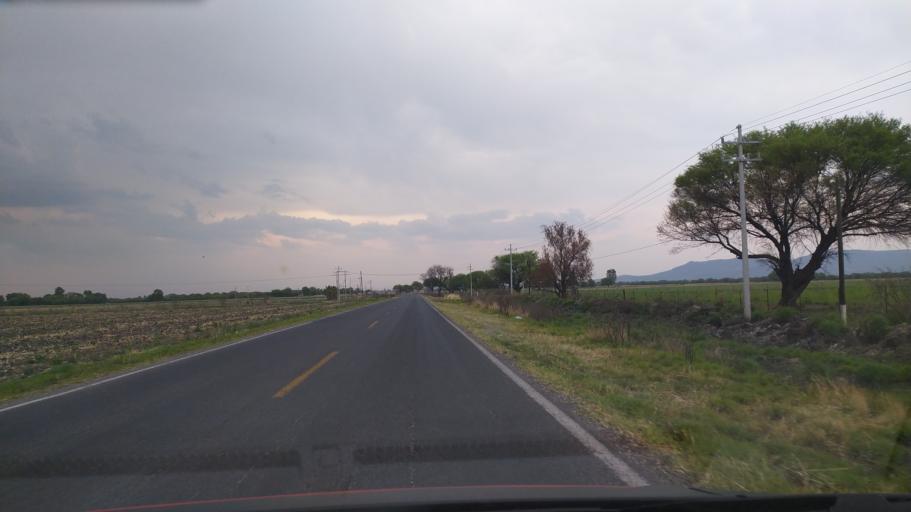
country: MX
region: Guanajuato
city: Ciudad Manuel Doblado
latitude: 20.7586
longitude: -101.9182
